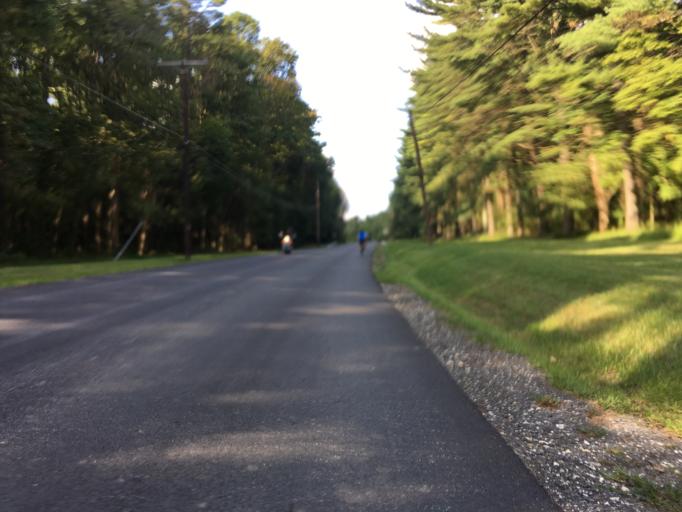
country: US
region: Pennsylvania
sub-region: York County
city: New Freedom
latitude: 39.6309
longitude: -76.7035
